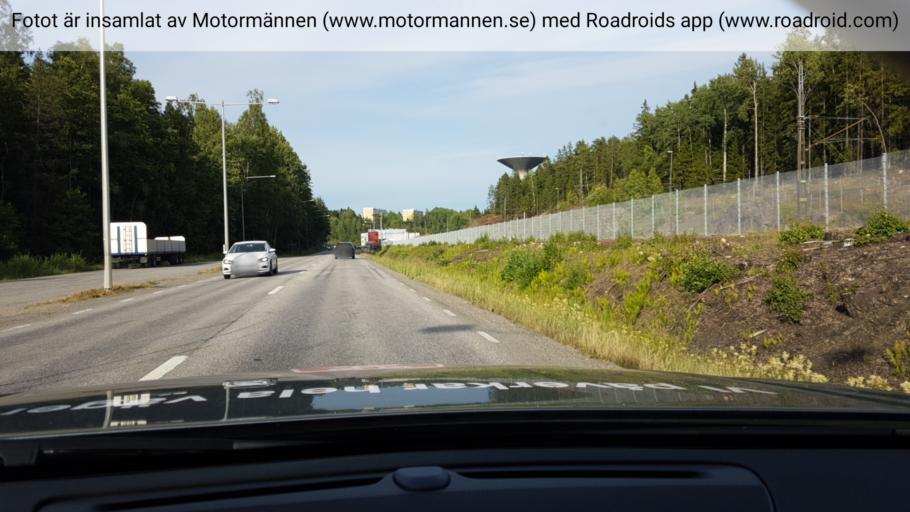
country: SE
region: Stockholm
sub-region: Botkyrka Kommun
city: Tullinge
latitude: 59.2126
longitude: 17.9314
